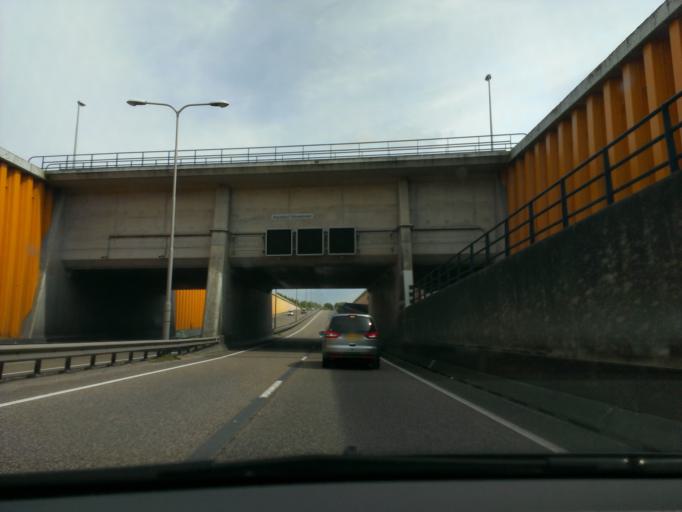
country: NL
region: Gelderland
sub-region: Gemeente Harderwijk
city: Harderwijk
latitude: 52.3611
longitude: 5.6179
